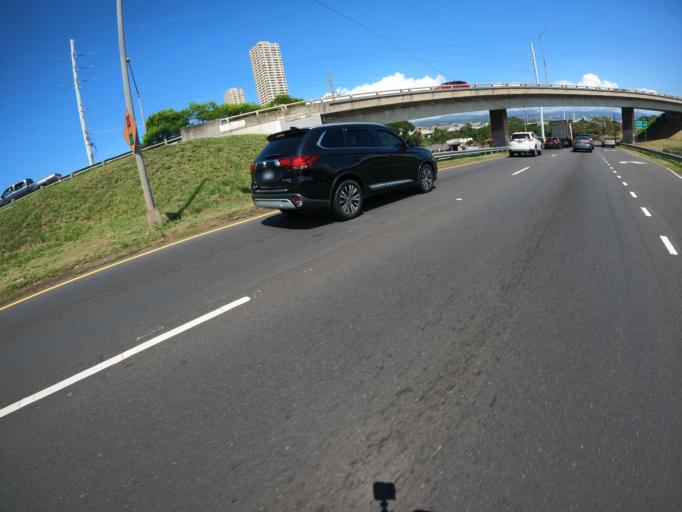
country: US
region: Hawaii
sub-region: Honolulu County
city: Pearl City, Manana
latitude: 21.3960
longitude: -157.9821
